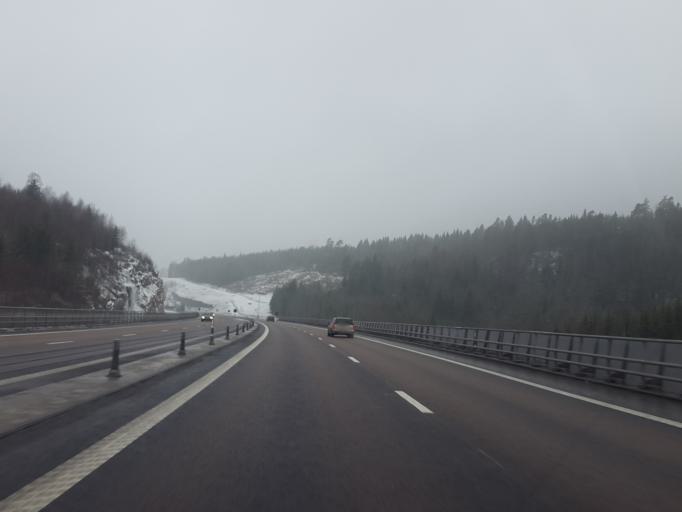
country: SE
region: Vaestra Goetaland
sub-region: Ulricehamns Kommun
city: Ulricehamn
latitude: 57.8122
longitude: 13.4061
